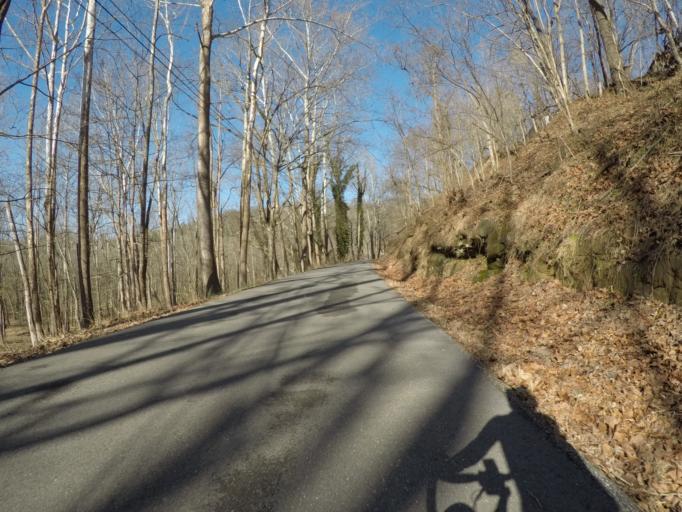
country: US
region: Kentucky
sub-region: Boyd County
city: Catlettsburg
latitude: 38.4181
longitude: -82.6080
